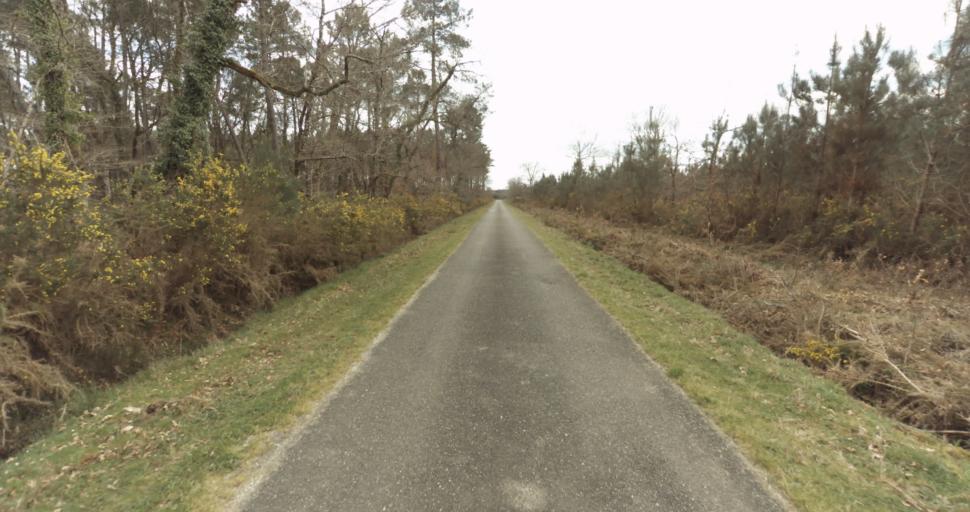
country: FR
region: Aquitaine
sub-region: Departement des Landes
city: Roquefort
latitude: 44.0829
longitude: -0.4412
